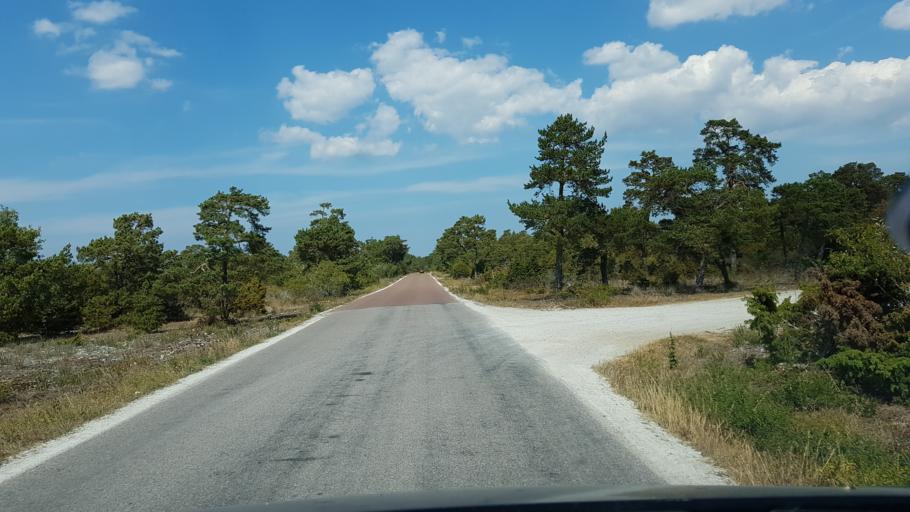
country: SE
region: Gotland
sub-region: Gotland
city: Visby
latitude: 57.6802
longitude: 18.3639
